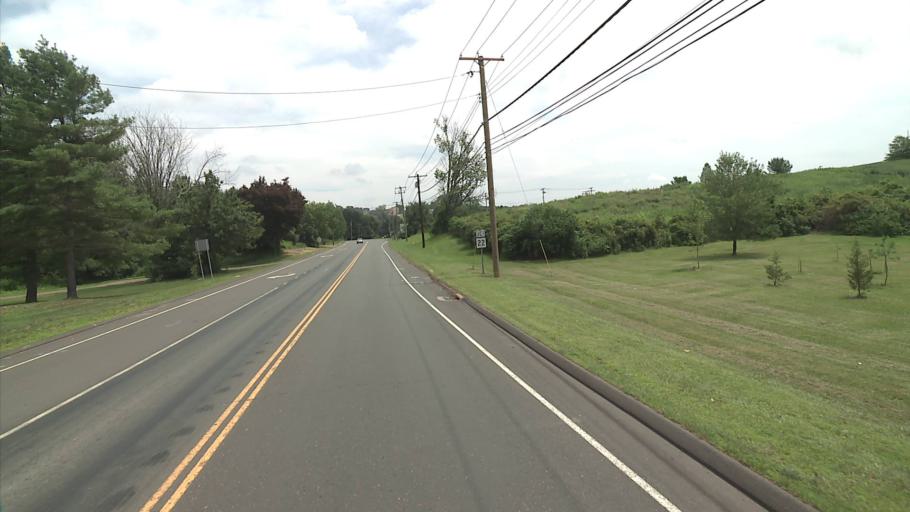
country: US
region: Connecticut
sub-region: New Haven County
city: North Branford
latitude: 41.3325
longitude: -72.7992
